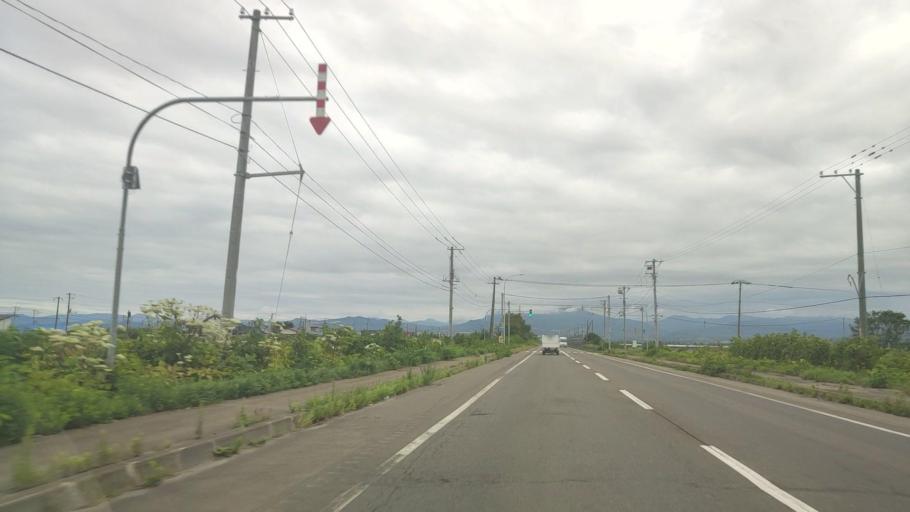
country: JP
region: Hokkaido
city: Nanae
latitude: 42.3136
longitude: 140.2736
